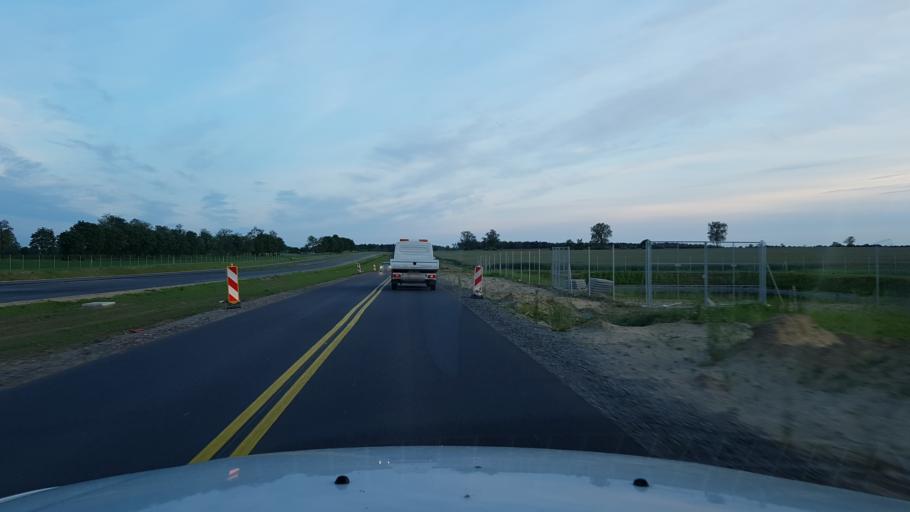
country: PL
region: West Pomeranian Voivodeship
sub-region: Powiat goleniowski
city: Nowogard
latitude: 53.7088
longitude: 15.1737
